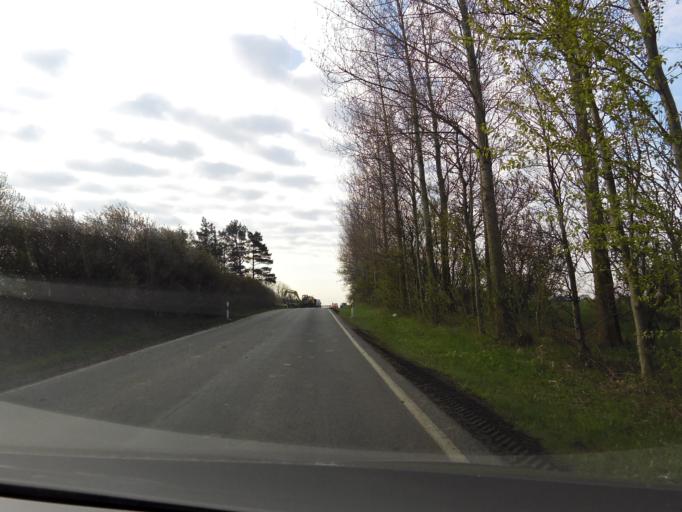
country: DE
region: Mecklenburg-Vorpommern
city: Trinwillershagen
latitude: 54.3156
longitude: 12.5842
